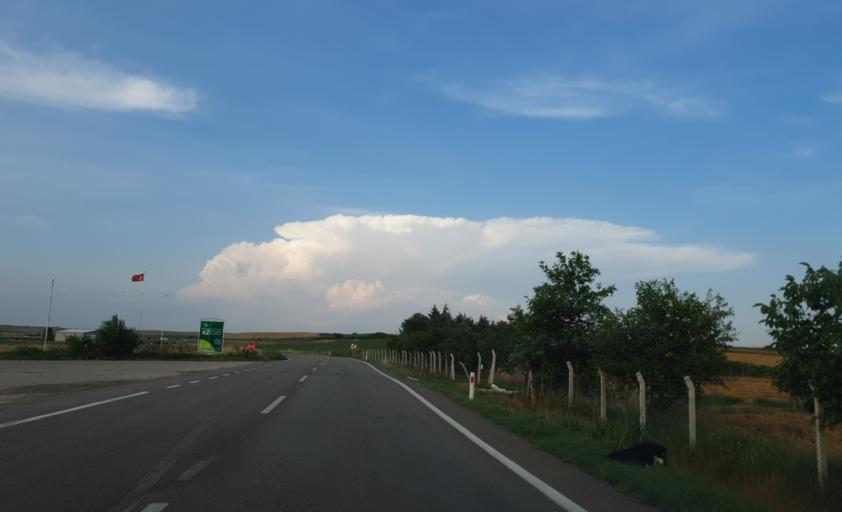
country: TR
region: Tekirdag
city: Hayrabolu
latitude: 41.2350
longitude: 27.1279
